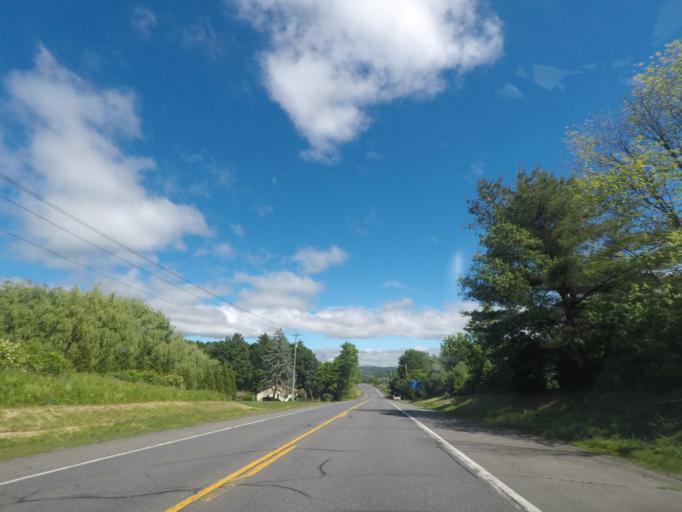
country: US
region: New York
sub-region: Columbia County
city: Philmont
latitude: 42.1791
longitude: -73.6028
